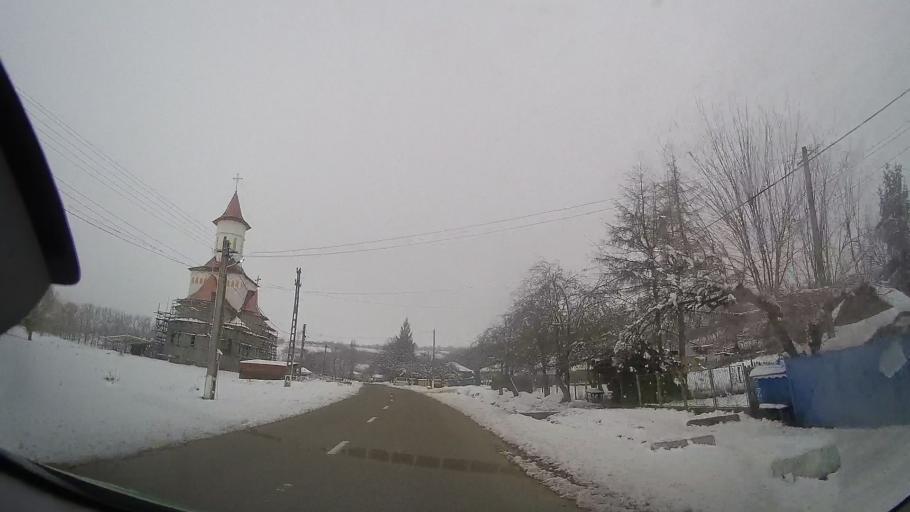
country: RO
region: Neamt
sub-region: Comuna Oniceni
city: Oniceni
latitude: 46.8065
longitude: 27.1731
